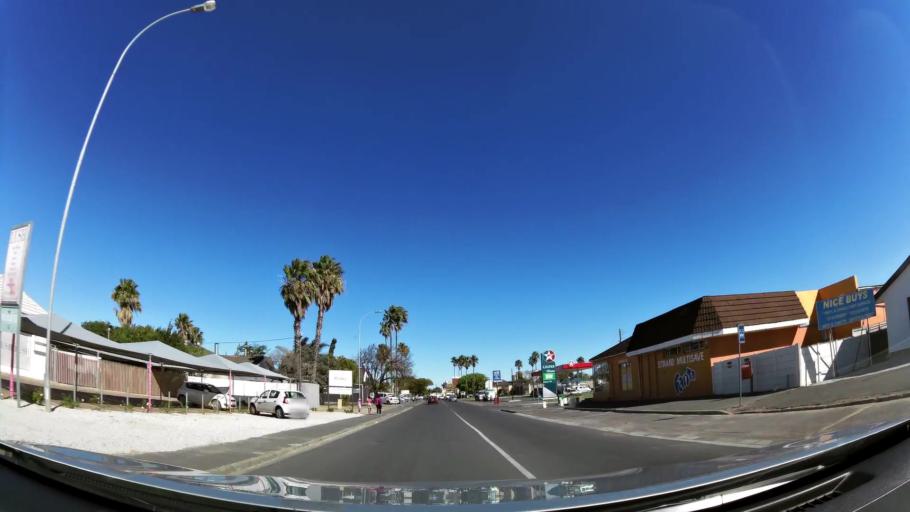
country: ZA
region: Western Cape
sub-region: Cape Winelands District Municipality
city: Stellenbosch
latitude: -34.1100
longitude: 18.8359
